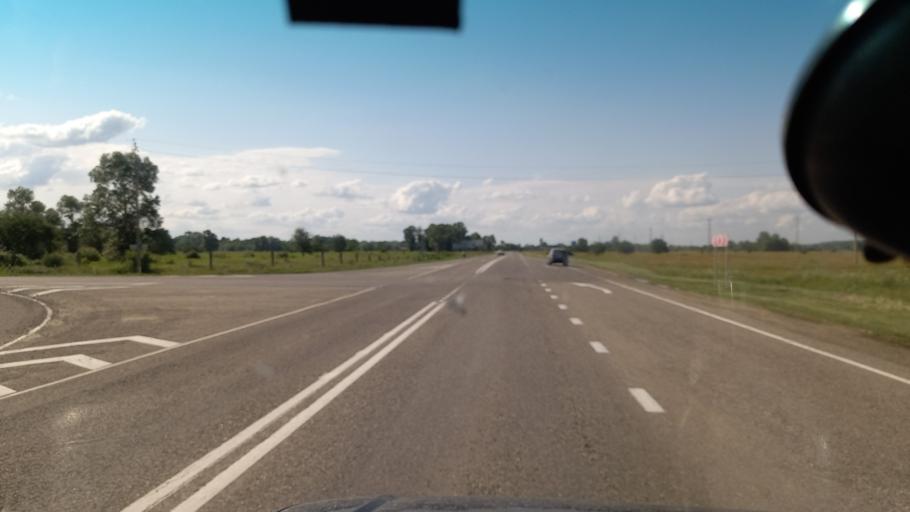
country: RU
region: Krasnodarskiy
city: Mostovskoy
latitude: 44.4049
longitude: 40.8350
